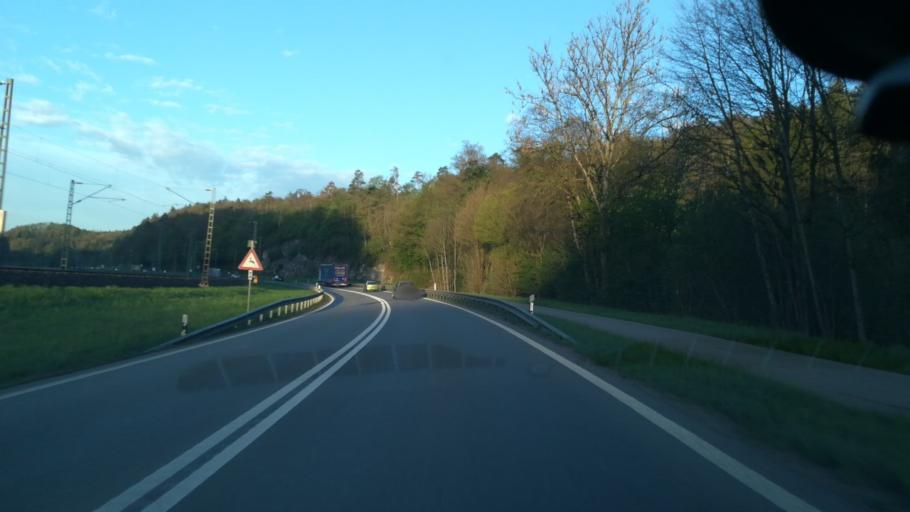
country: CH
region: Schaffhausen
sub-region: Bezirk Reiat
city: Stetten
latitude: 47.7360
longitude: 8.6815
